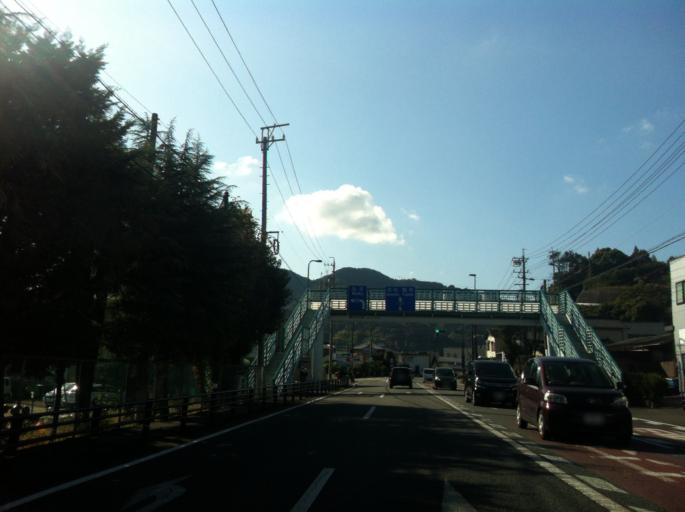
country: JP
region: Shizuoka
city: Shizuoka-shi
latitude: 34.9488
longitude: 138.3588
